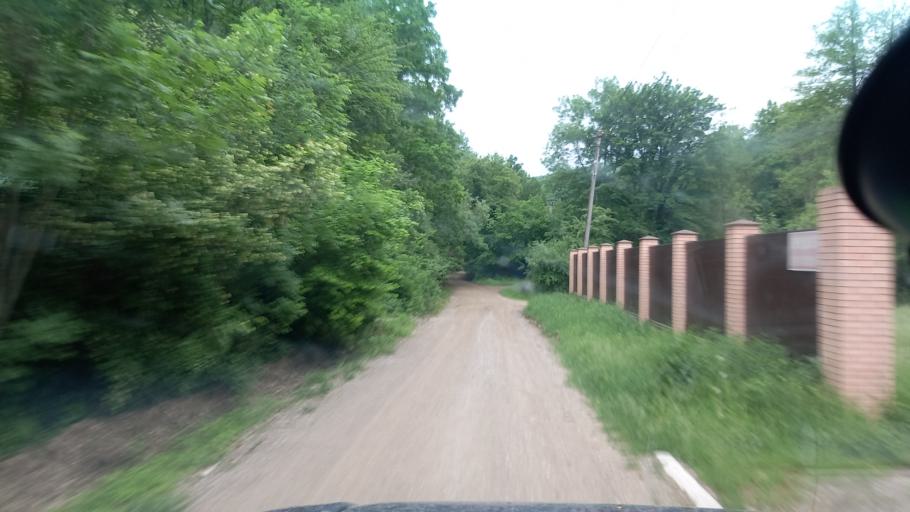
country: RU
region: Krasnodarskiy
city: Azovskaya
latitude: 44.6361
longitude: 38.6193
